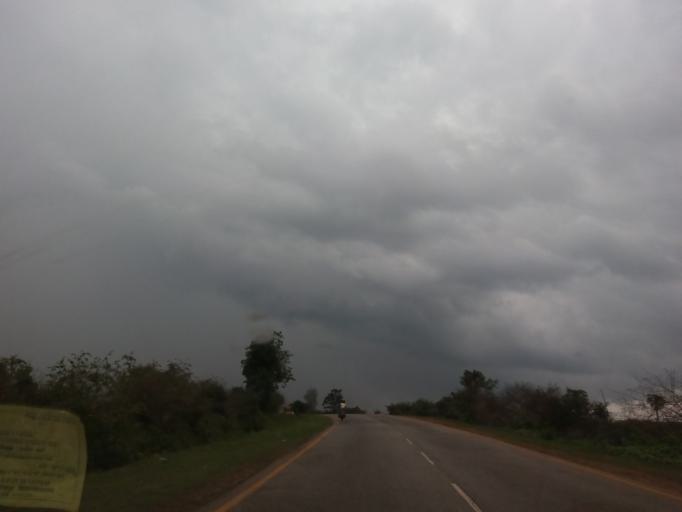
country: IN
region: Karnataka
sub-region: Hassan
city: Hassan
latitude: 13.0919
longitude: 76.0354
